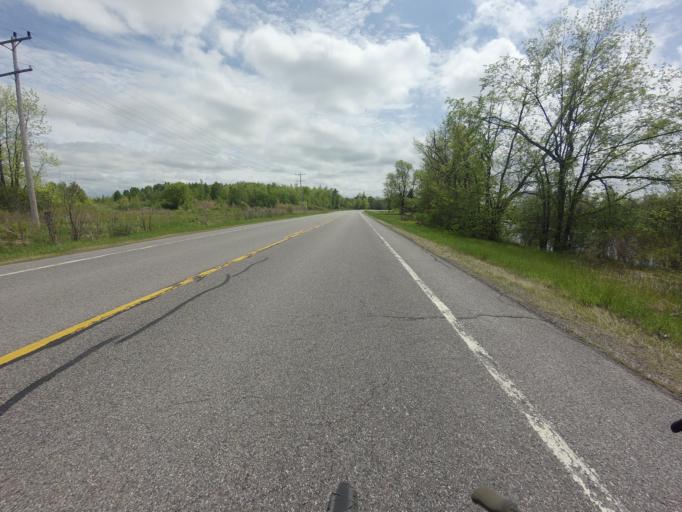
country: CA
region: Ontario
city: Cornwall
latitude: 44.9634
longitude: -74.6657
